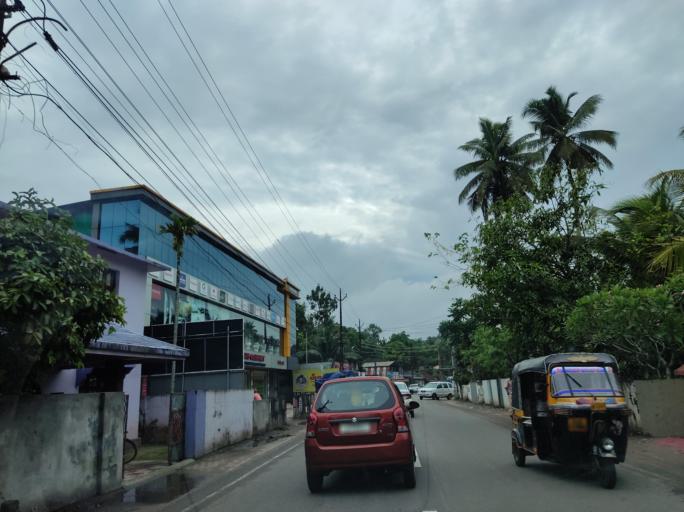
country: IN
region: Kerala
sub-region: Alappuzha
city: Mavelikara
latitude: 9.2522
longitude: 76.4848
